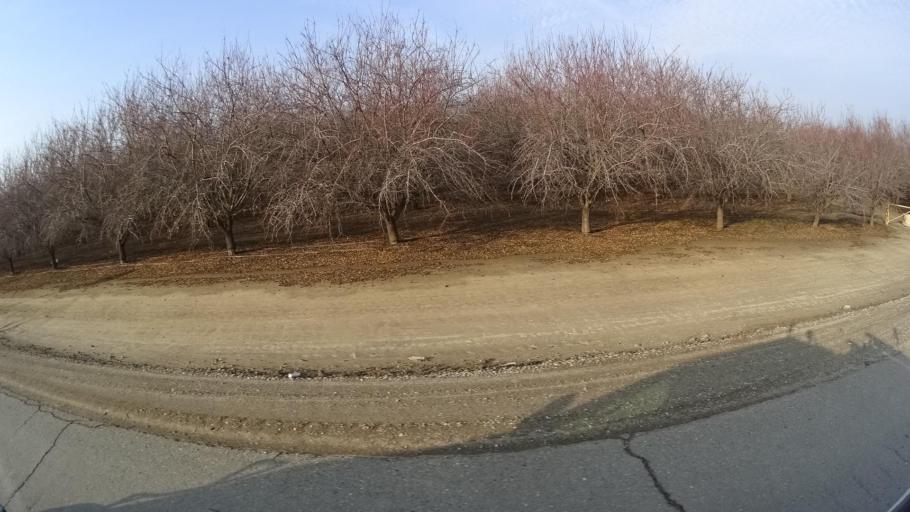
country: US
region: California
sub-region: Kern County
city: Weedpatch
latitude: 35.2050
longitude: -118.9146
